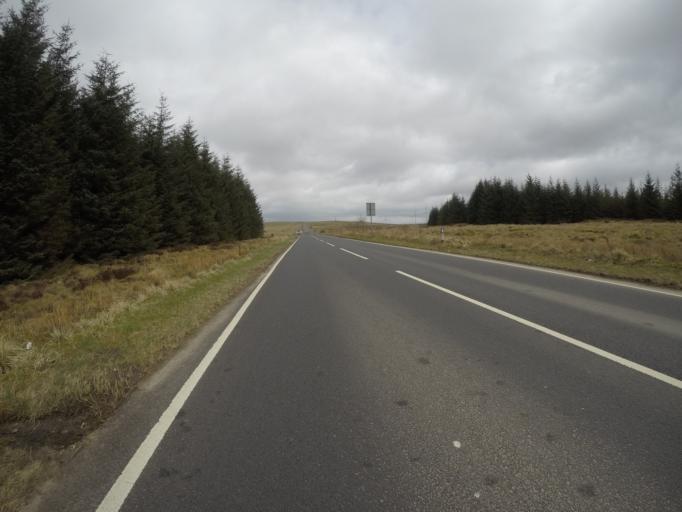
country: GB
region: Scotland
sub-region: East Renfrewshire
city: Newton Mearns
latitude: 55.7064
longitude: -4.3647
